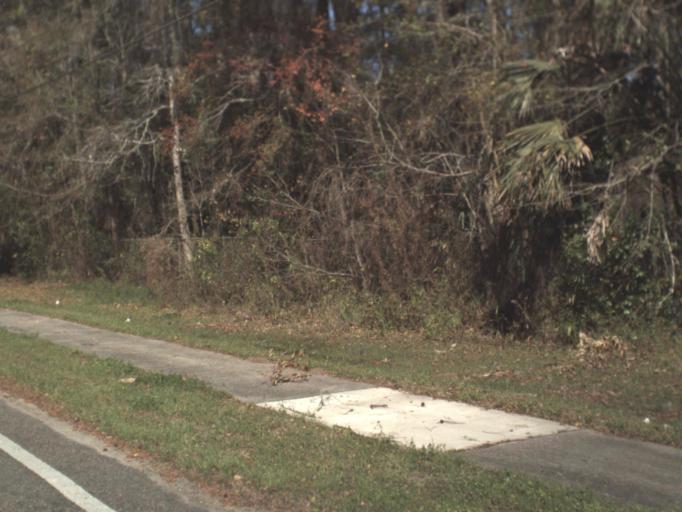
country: US
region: Florida
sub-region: Leon County
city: Tallahassee
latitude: 30.4126
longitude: -84.3277
